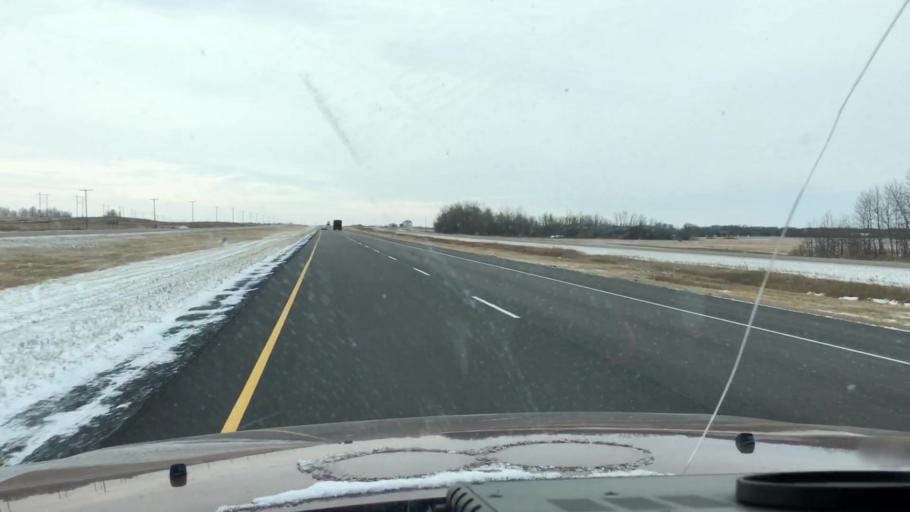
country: CA
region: Saskatchewan
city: Saskatoon
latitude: 51.9377
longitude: -106.5389
